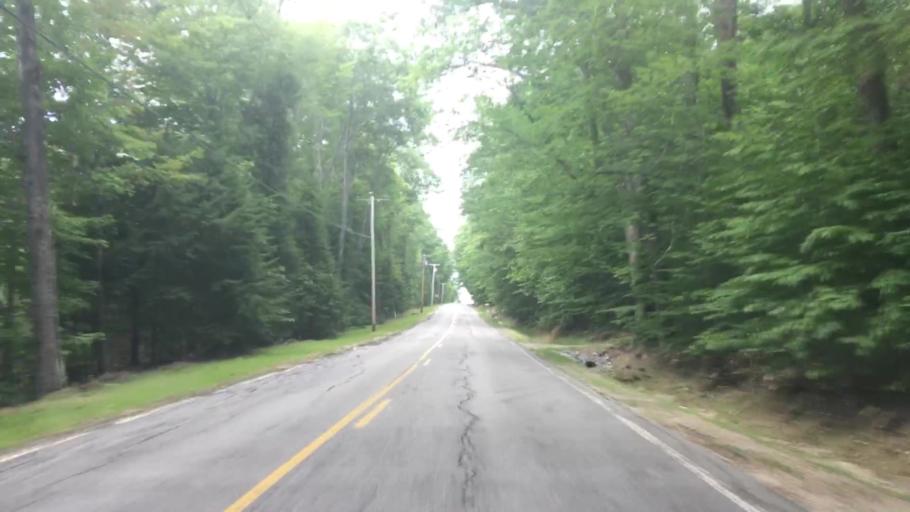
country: US
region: Maine
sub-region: Oxford County
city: Oxford
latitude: 44.0187
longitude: -70.5276
